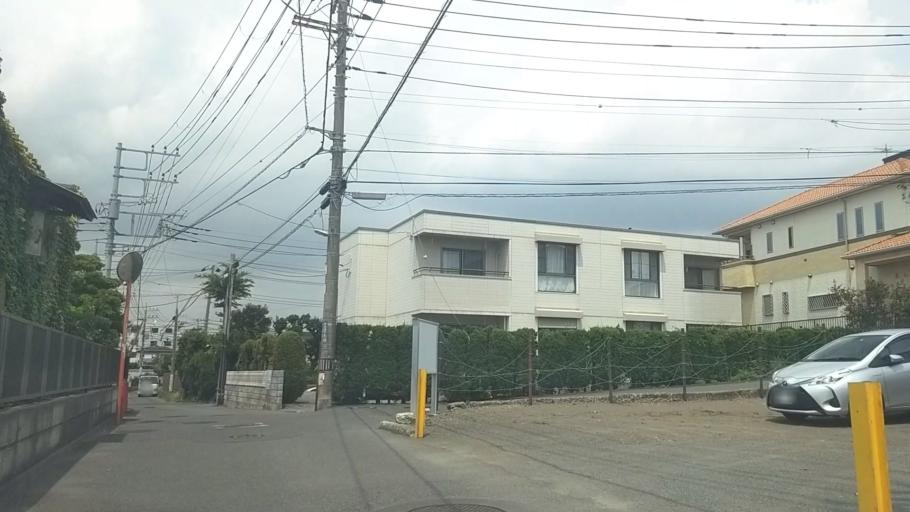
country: JP
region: Kanagawa
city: Chigasaki
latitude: 35.3547
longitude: 139.3978
